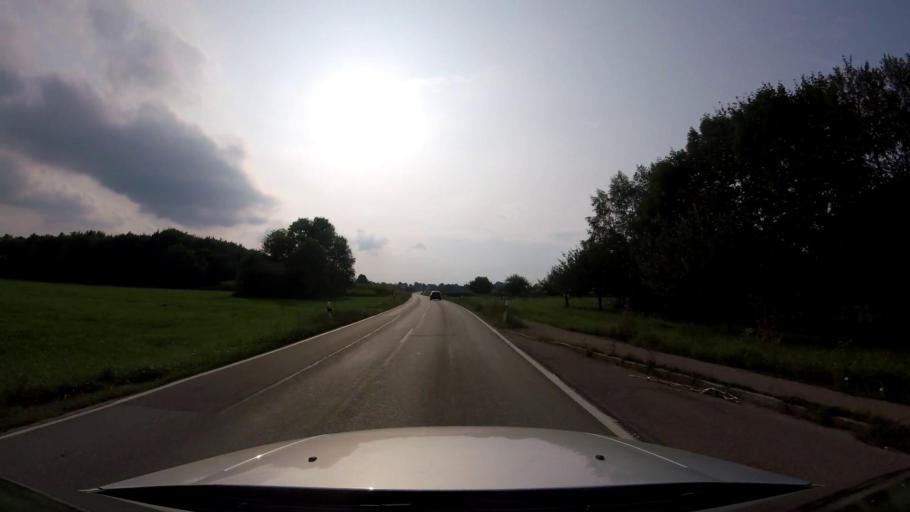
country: DE
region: Baden-Wuerttemberg
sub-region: Regierungsbezirk Stuttgart
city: Alfdorf
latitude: 48.8420
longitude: 9.7387
